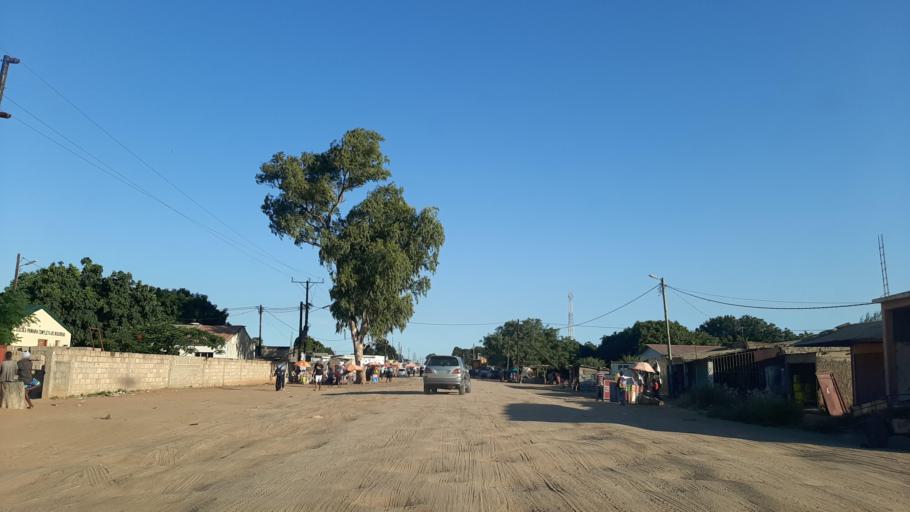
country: MZ
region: Maputo City
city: Maputo
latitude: -25.7357
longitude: 32.5379
